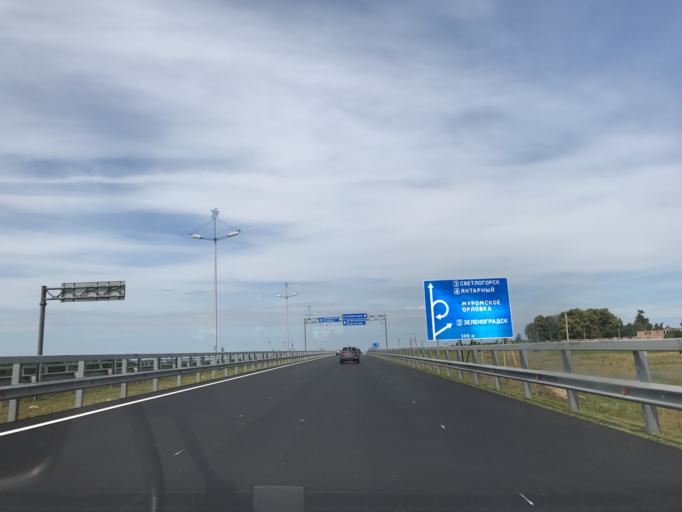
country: RU
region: Kaliningrad
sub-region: Zelenogradskiy Rayon
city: Zelenogradsk
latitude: 54.9037
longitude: 20.5079
